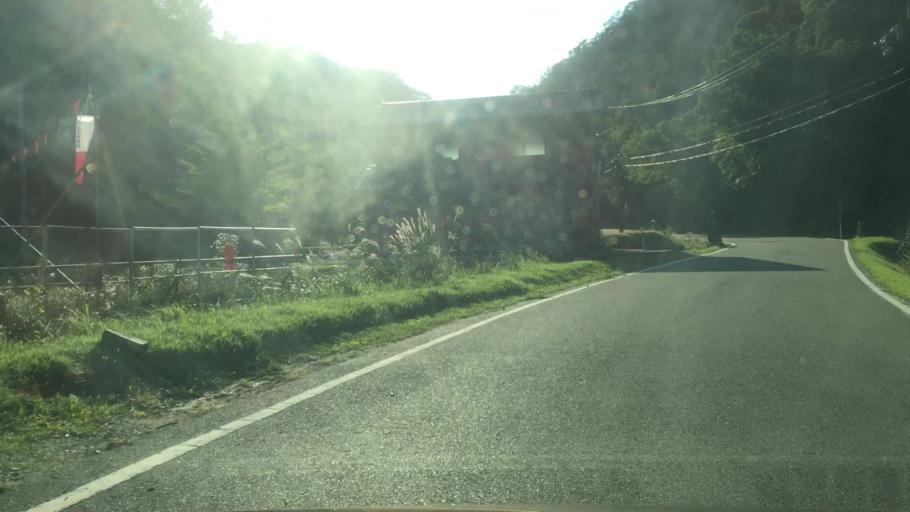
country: JP
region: Hyogo
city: Toyooka
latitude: 35.6119
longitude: 134.8426
